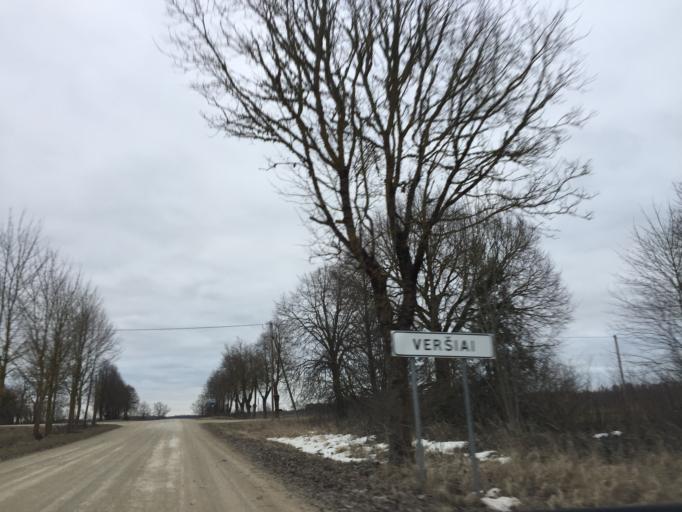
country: LT
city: Zagare
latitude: 56.3139
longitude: 23.2479
